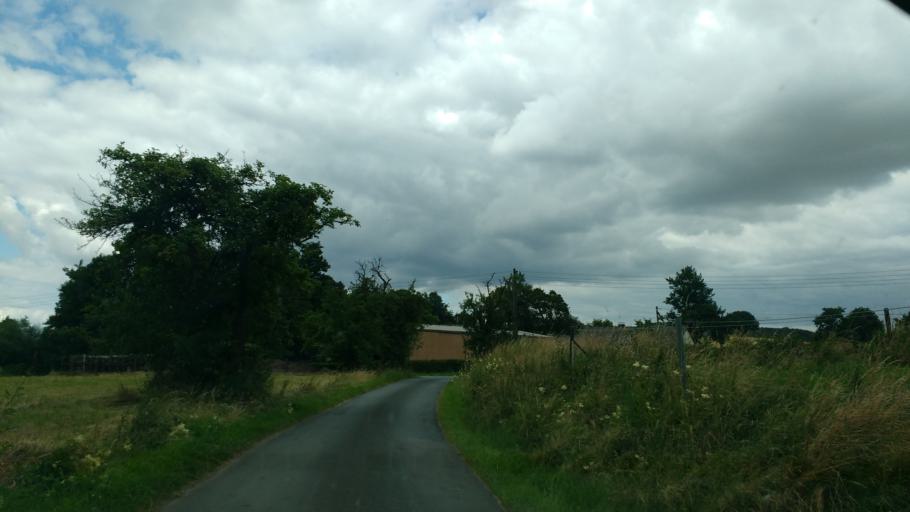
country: DE
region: North Rhine-Westphalia
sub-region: Regierungsbezirk Detmold
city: Horn
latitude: 51.9103
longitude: 8.9275
